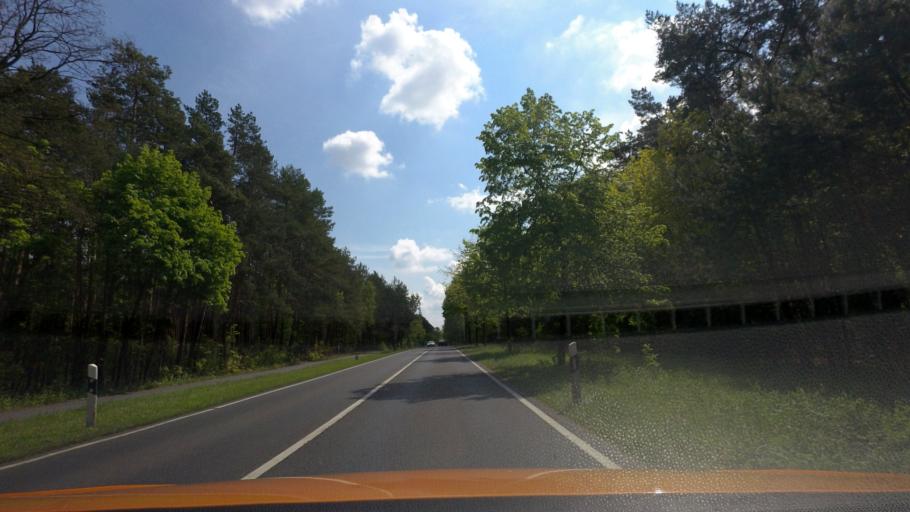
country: DE
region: Brandenburg
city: Zeuthen
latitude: 52.3969
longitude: 13.6090
